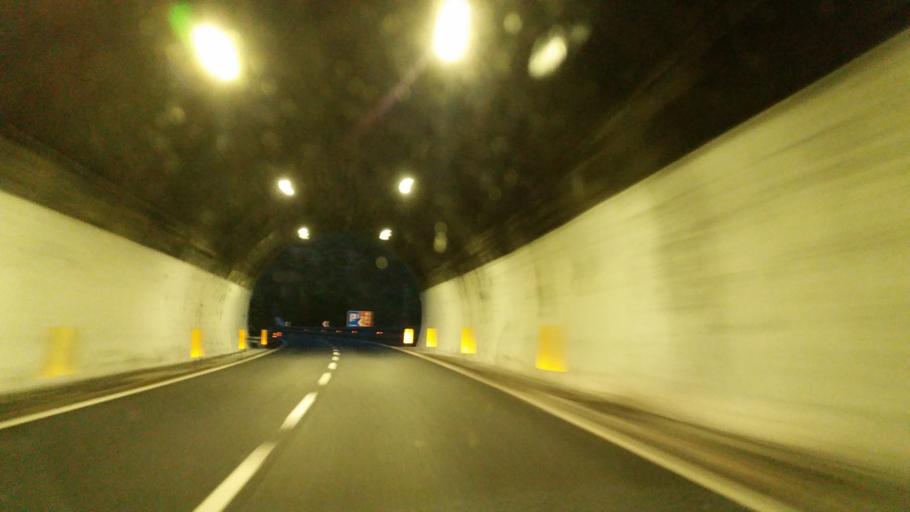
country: IT
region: Liguria
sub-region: Provincia di Imperia
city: Imperia
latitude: 43.9001
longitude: 8.0447
